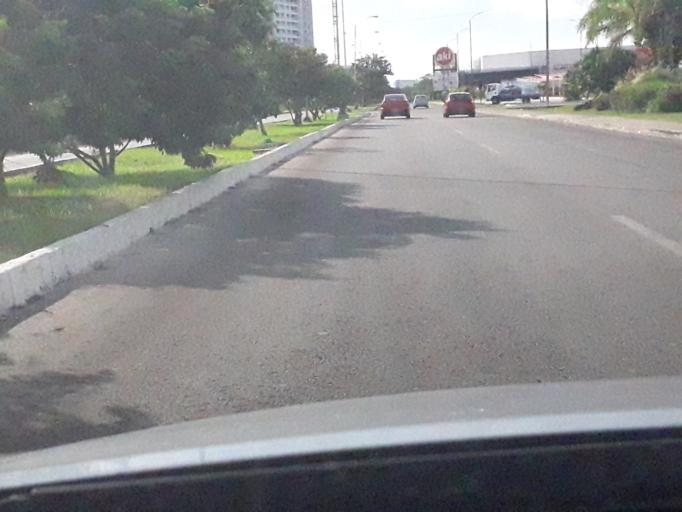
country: MX
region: Yucatan
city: Merida
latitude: 21.0375
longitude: -89.6117
